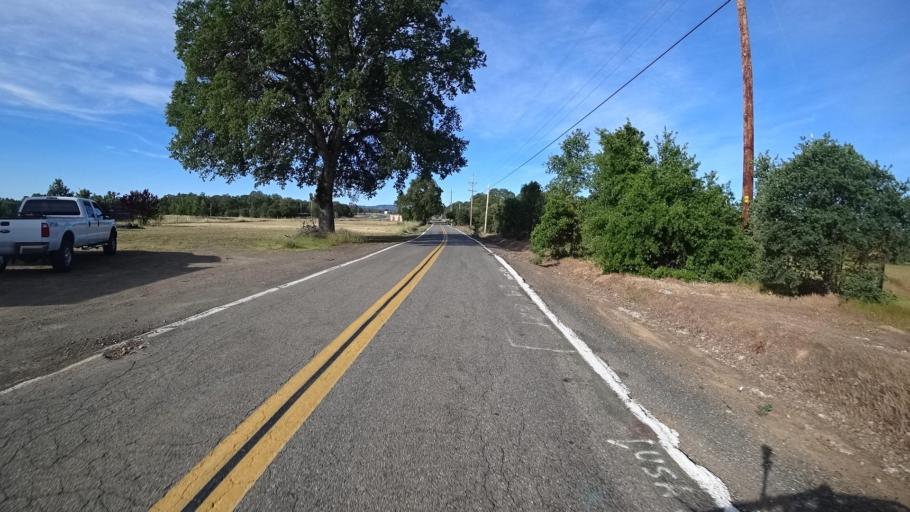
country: US
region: California
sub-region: Lake County
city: North Lakeport
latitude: 39.0843
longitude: -122.9281
